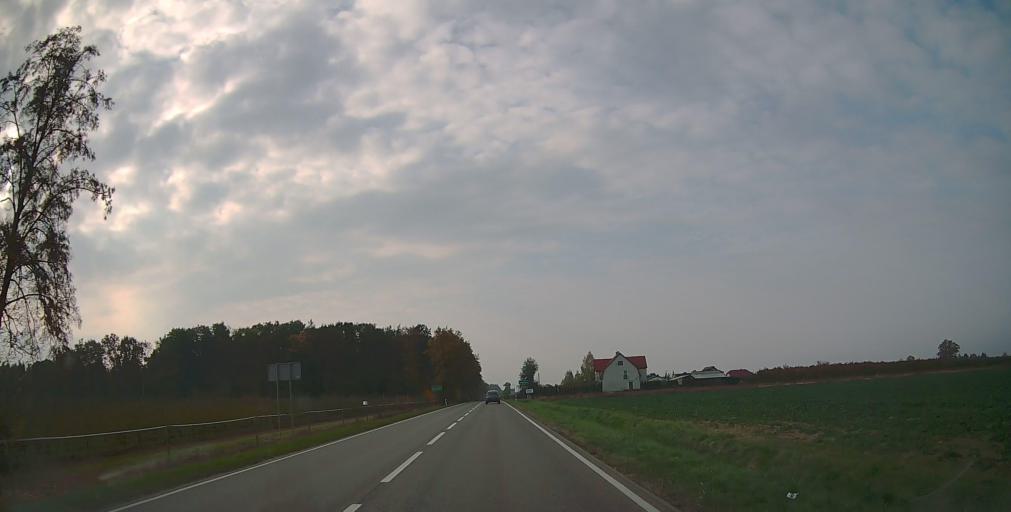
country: PL
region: Masovian Voivodeship
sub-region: Powiat grojecki
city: Belsk Duzy
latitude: 51.8000
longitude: 20.7887
